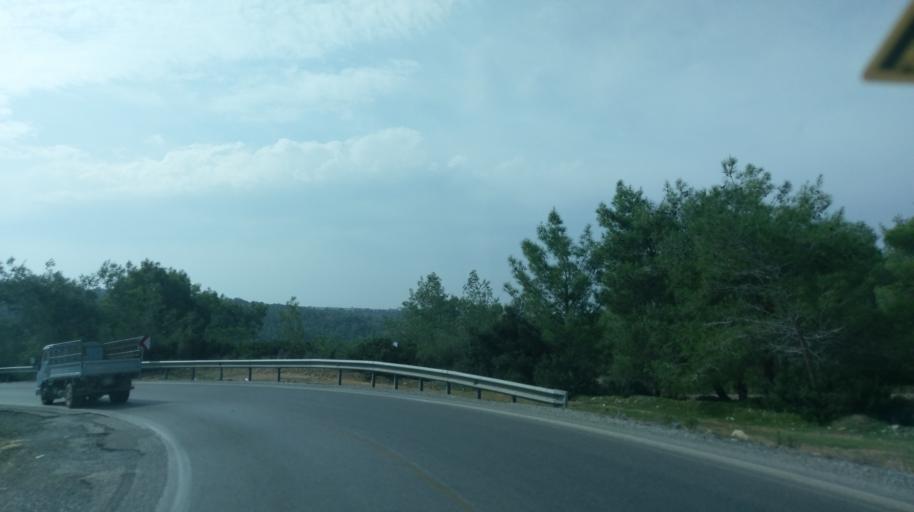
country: CY
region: Lefkosia
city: Morfou
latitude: 35.2600
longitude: 33.0379
